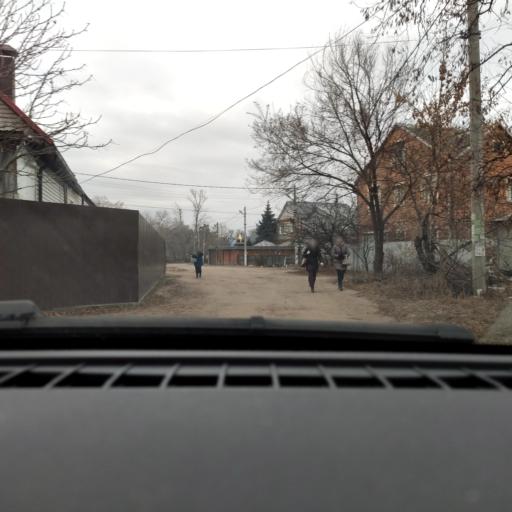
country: RU
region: Voronezj
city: Voronezh
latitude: 51.7330
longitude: 39.2648
